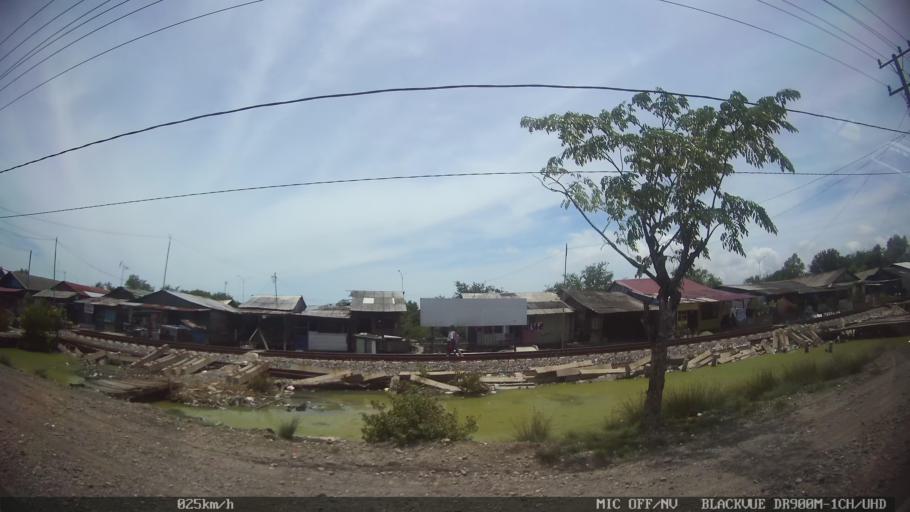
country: ID
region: North Sumatra
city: Belawan
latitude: 3.7658
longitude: 98.6829
